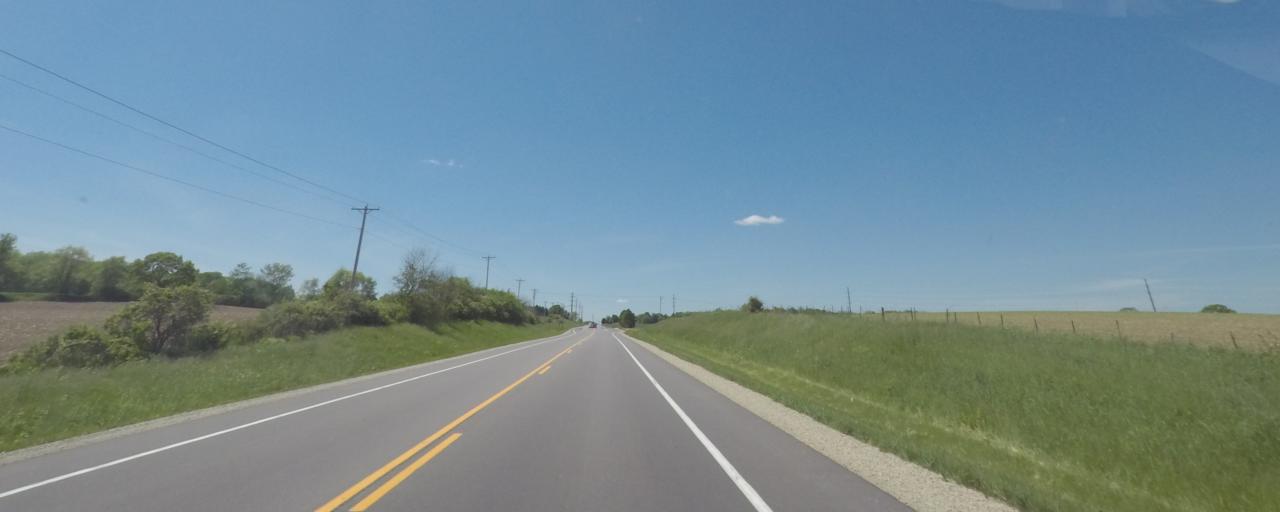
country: US
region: Wisconsin
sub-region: Dane County
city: Fitchburg
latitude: 42.9621
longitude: -89.4826
